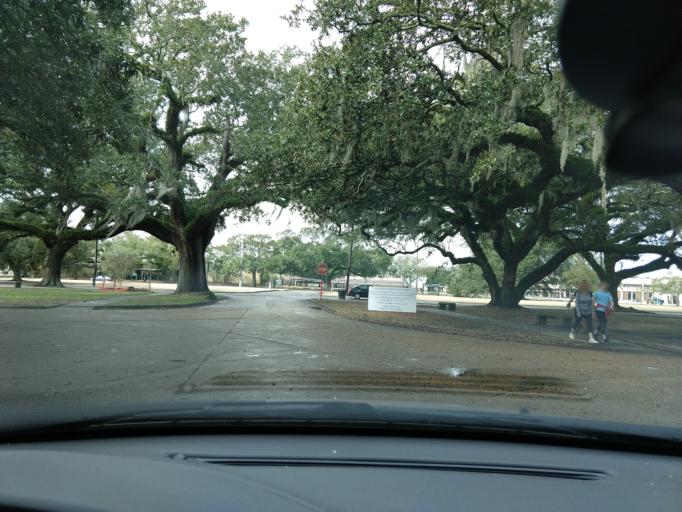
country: US
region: Louisiana
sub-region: Orleans Parish
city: New Orleans
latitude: 29.9865
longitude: -90.1013
